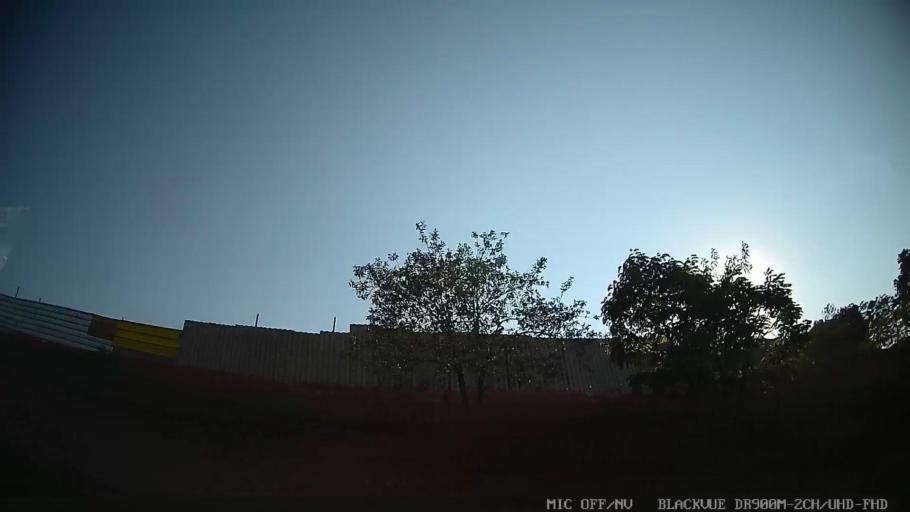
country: BR
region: Sao Paulo
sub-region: Itatiba
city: Itatiba
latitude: -22.9898
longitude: -46.8371
